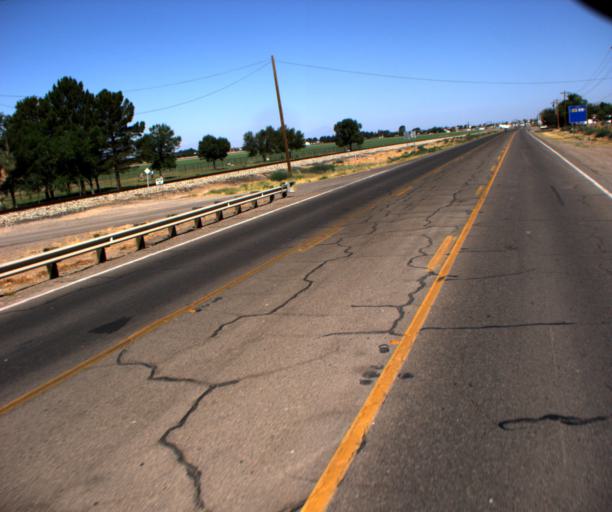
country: US
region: Arizona
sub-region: Graham County
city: Safford
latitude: 32.8248
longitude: -109.6908
